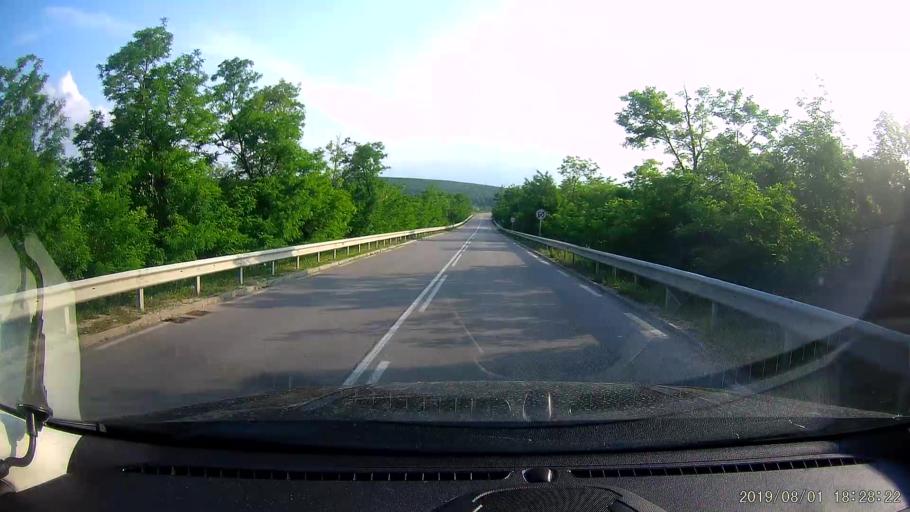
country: BG
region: Shumen
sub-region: Obshtina Venets
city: Venets
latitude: 43.5762
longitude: 26.9657
